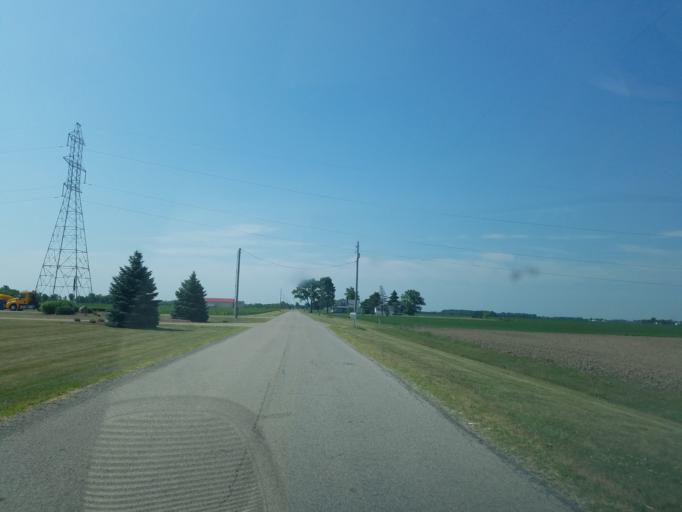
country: US
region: Ohio
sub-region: Van Wert County
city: Convoy
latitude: 40.9284
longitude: -84.6296
